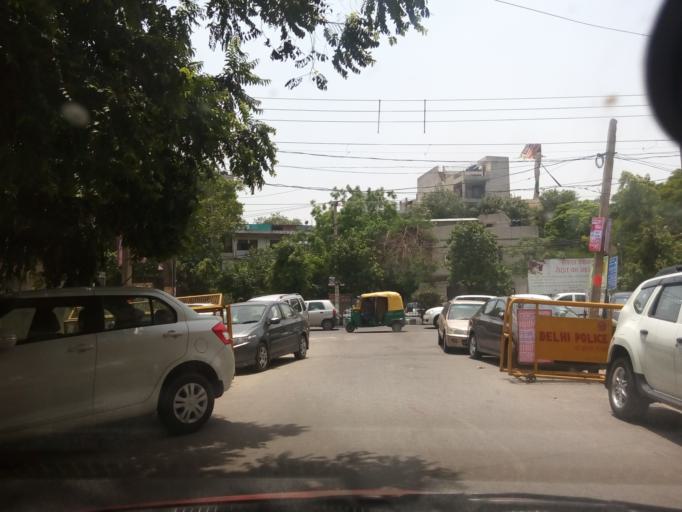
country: IN
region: NCT
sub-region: Central Delhi
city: Karol Bagh
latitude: 28.6924
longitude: 77.1748
